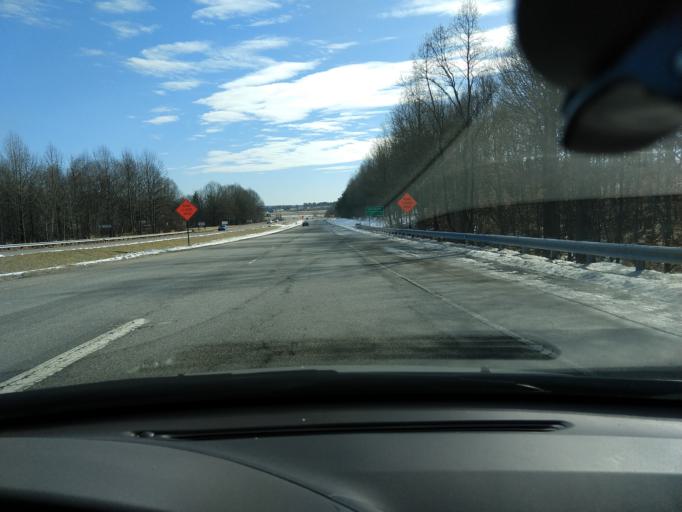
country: US
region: North Carolina
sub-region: Guilford County
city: Oak Ridge
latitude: 36.1083
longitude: -79.9603
